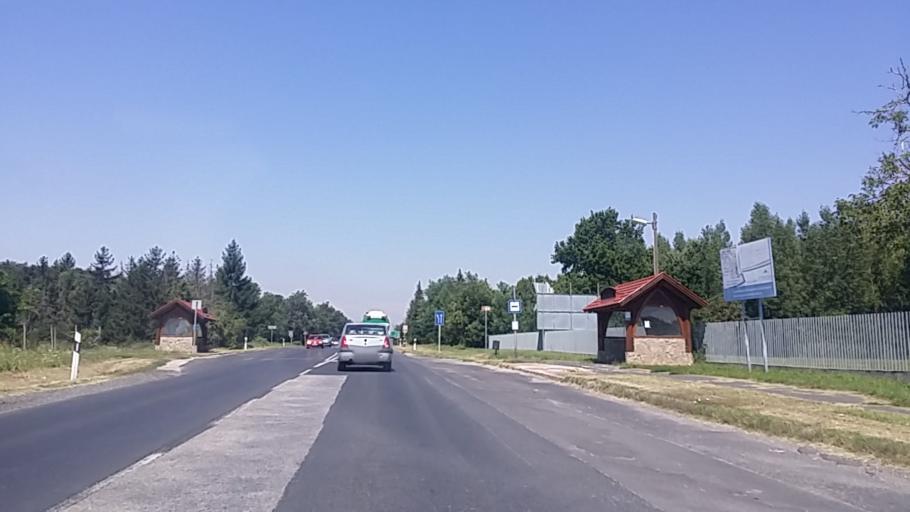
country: HU
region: Zala
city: Keszthely
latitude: 46.7789
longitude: 17.2241
